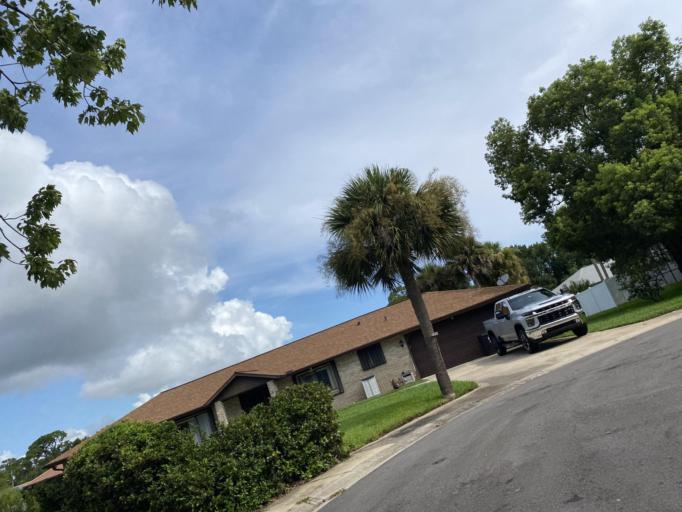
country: US
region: Florida
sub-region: Volusia County
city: Port Orange
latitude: 29.1364
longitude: -81.0013
